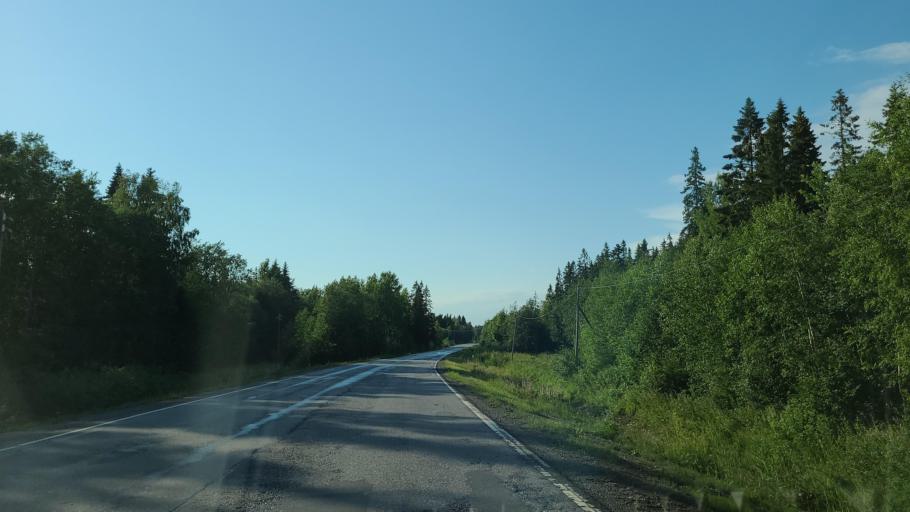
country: FI
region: Ostrobothnia
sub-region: Vaasa
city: Replot
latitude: 63.2110
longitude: 21.4329
